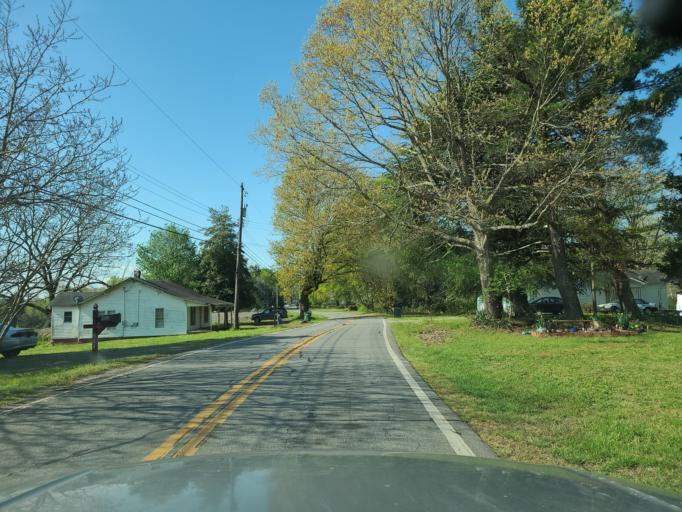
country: US
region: North Carolina
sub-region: Rutherford County
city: Spindale
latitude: 35.3759
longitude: -81.9231
